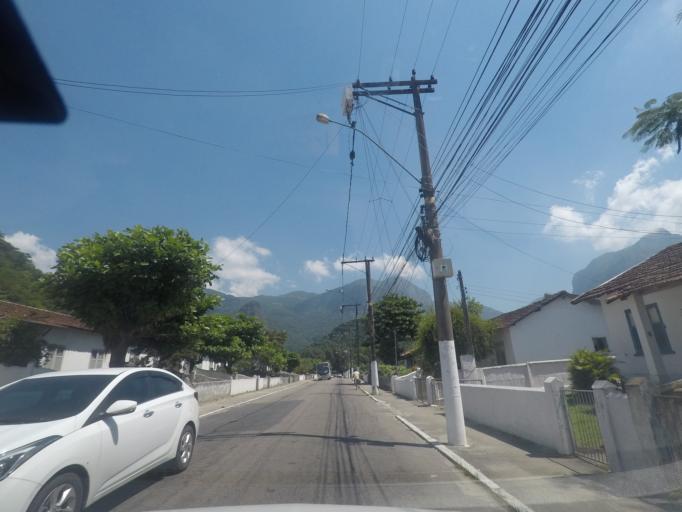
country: BR
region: Rio de Janeiro
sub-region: Petropolis
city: Petropolis
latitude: -22.5802
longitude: -43.1873
